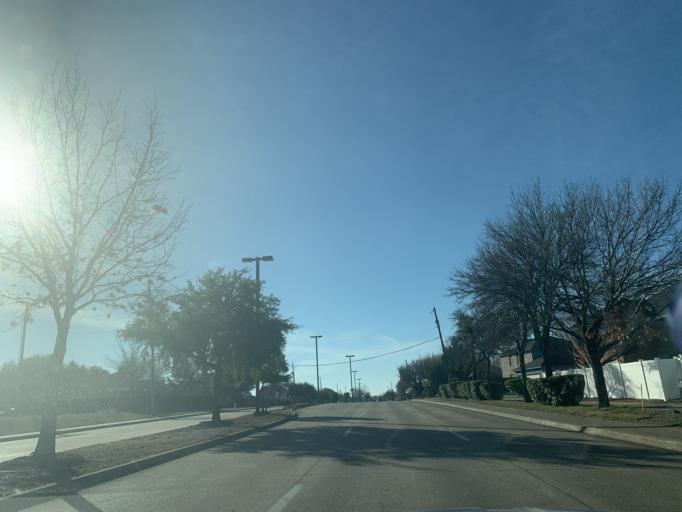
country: US
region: Texas
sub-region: Dallas County
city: DeSoto
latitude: 32.5865
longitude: -96.8400
